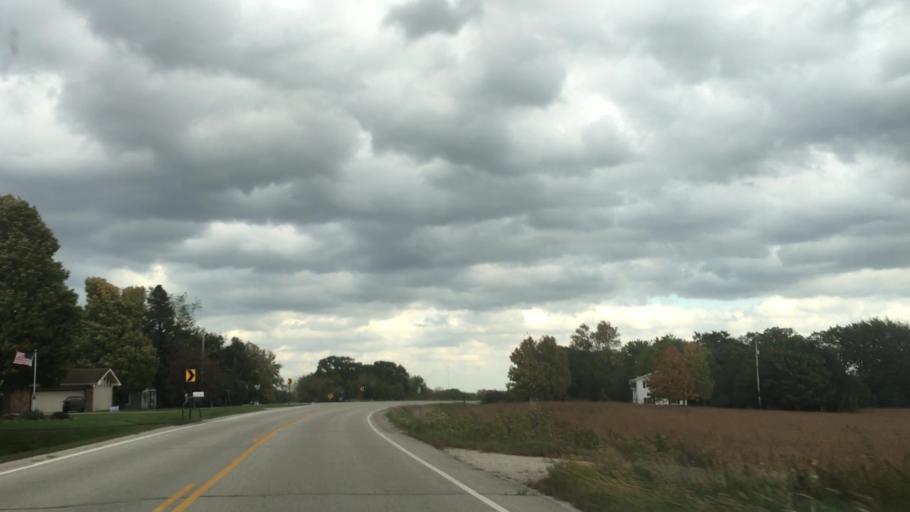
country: US
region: Minnesota
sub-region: Fillmore County
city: Preston
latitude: 43.7388
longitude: -92.1308
